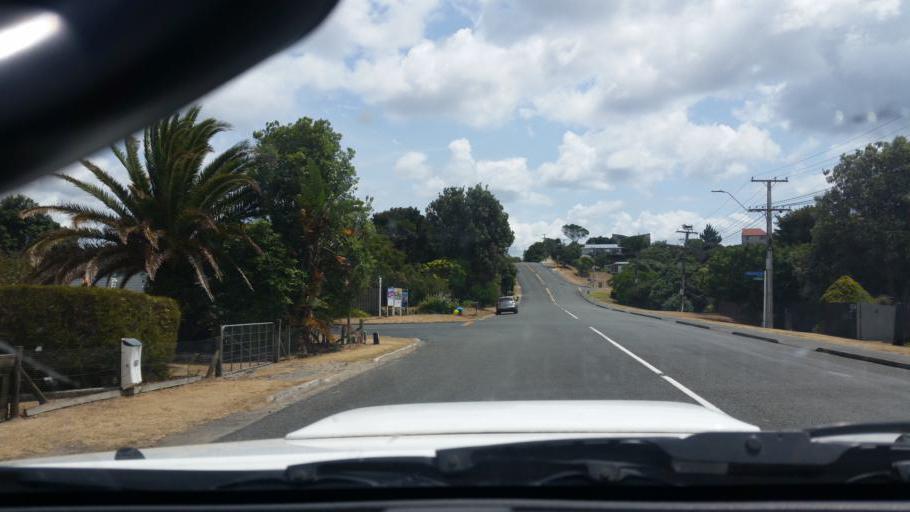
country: NZ
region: Auckland
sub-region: Auckland
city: Wellsford
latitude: -36.0899
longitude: 174.5842
